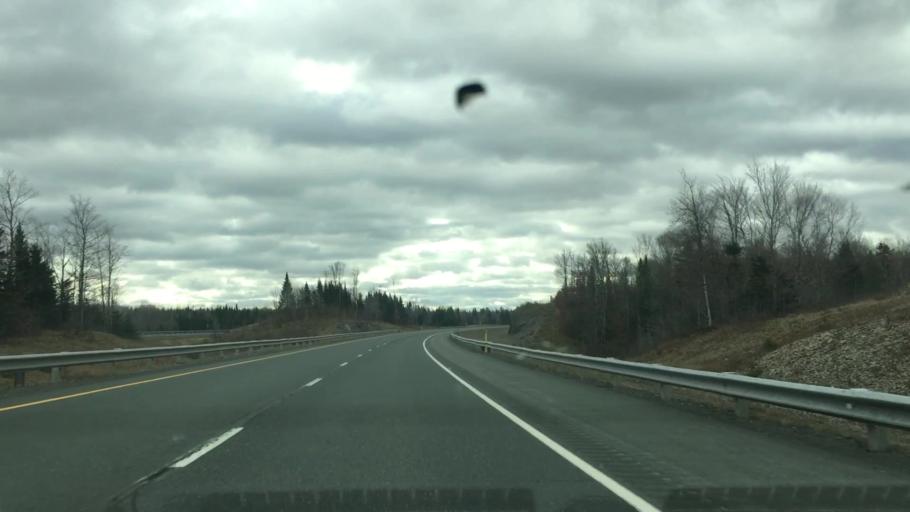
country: US
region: Maine
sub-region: Aroostook County
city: Easton
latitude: 46.6228
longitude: -67.7389
